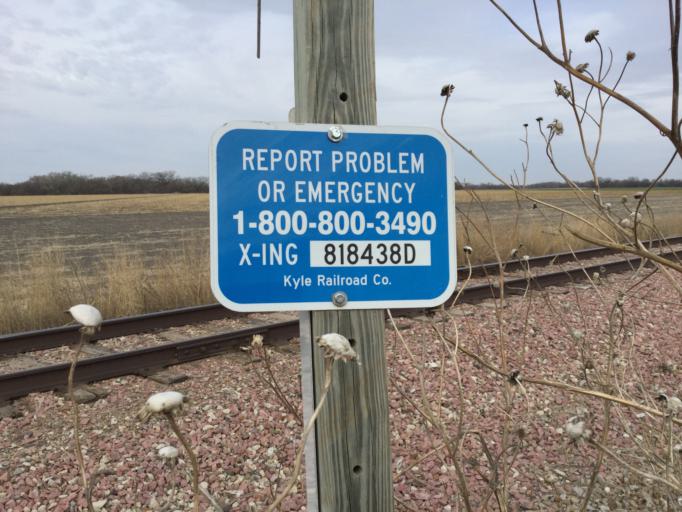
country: US
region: Kansas
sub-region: Ottawa County
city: Minneapolis
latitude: 39.3094
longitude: -97.7978
